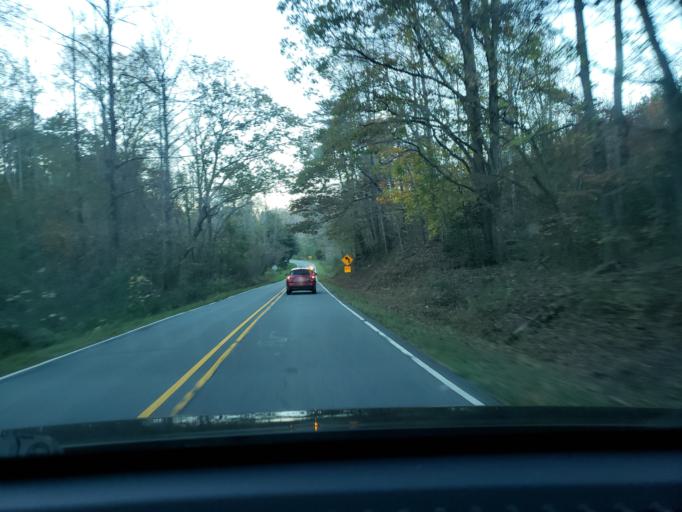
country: US
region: North Carolina
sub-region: Stokes County
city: Danbury
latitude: 36.4217
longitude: -80.2352
